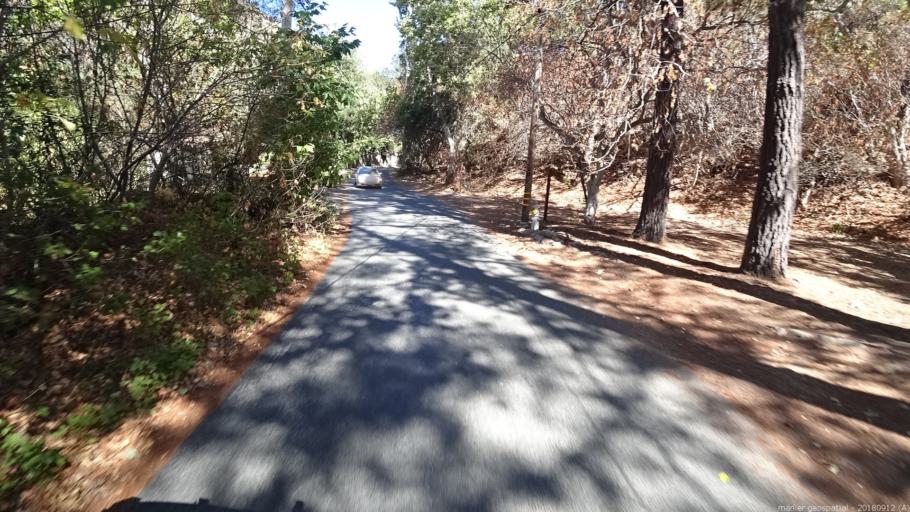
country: US
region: California
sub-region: Monterey County
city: Carmel Valley Village
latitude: 36.4660
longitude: -121.7236
